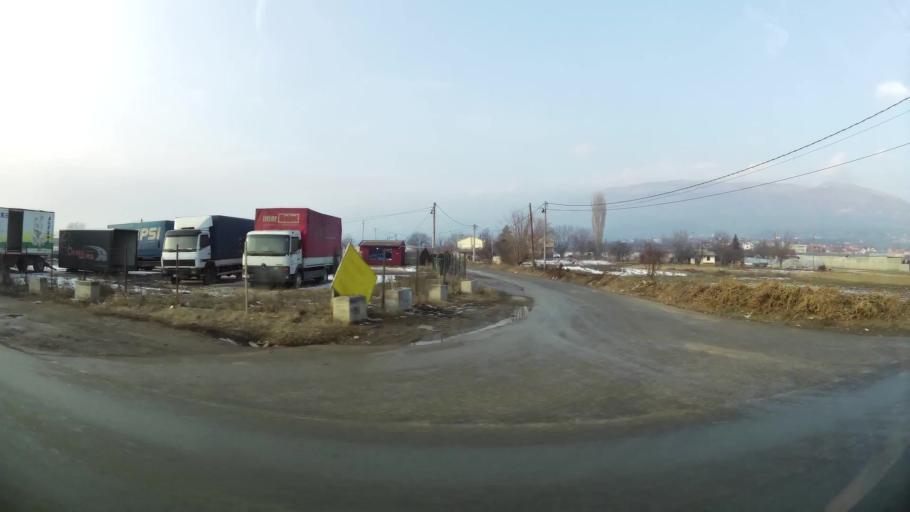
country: MK
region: Aracinovo
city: Arachinovo
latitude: 42.0218
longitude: 21.5458
